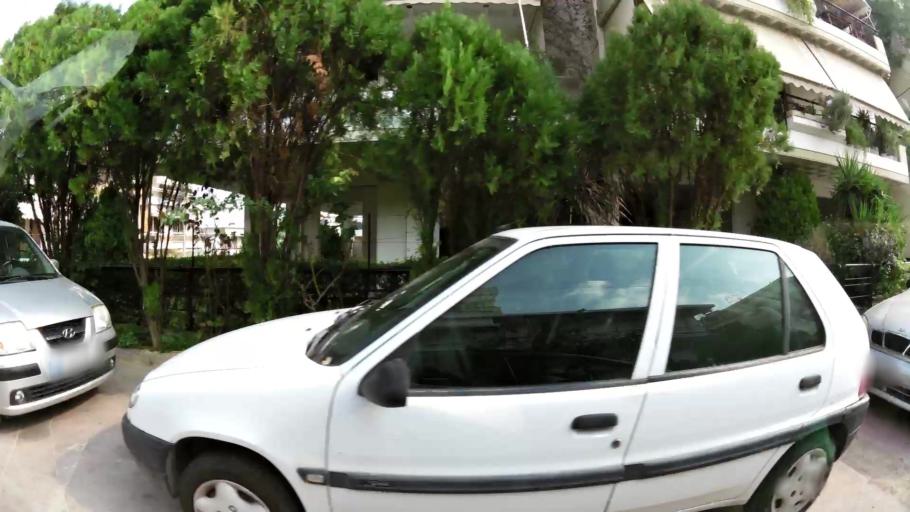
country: GR
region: Attica
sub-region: Nomarchia Athinas
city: Irakleio
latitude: 38.0546
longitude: 23.7677
